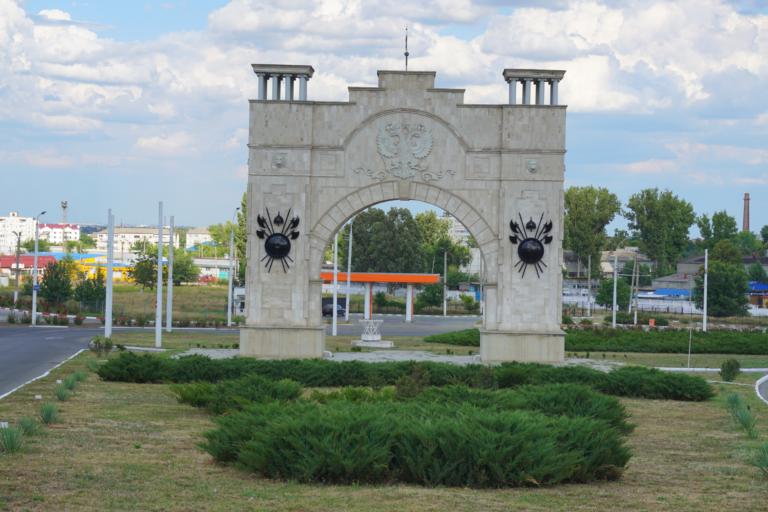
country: MD
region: Bender
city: Bender
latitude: 46.8442
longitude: 29.4691
